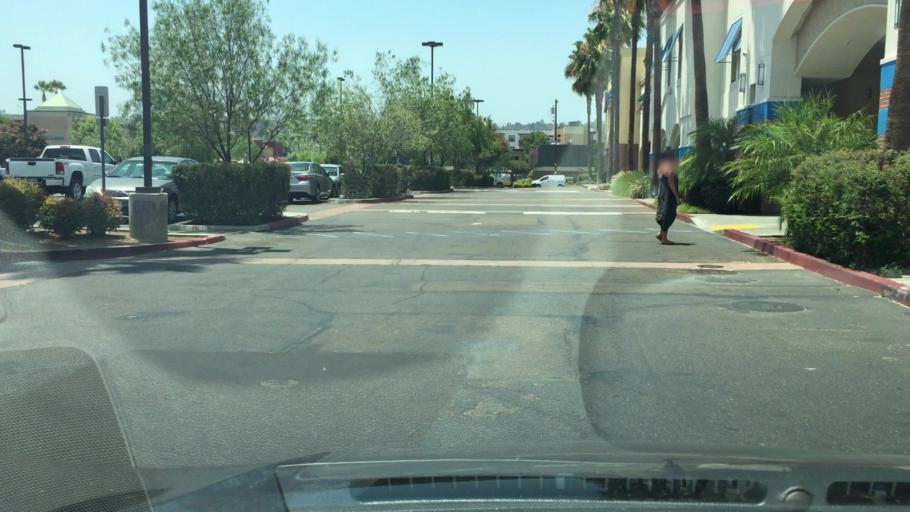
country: US
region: California
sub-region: San Diego County
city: El Cajon
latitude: 32.7959
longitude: -116.9635
